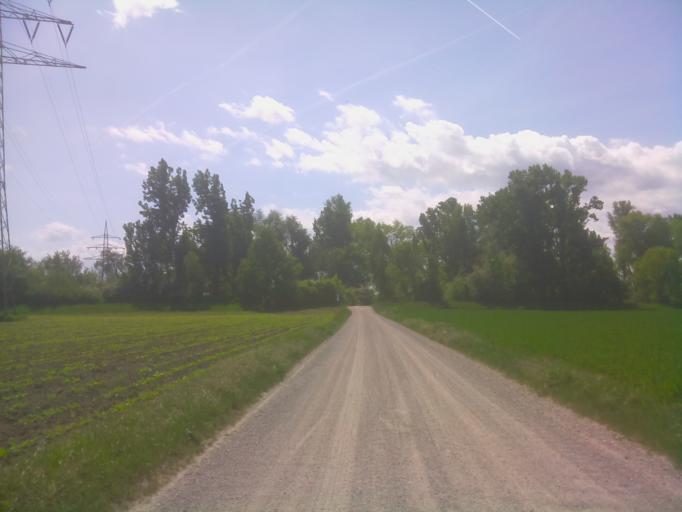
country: DE
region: Rheinland-Pfalz
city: Neuhofen
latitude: 49.4380
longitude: 8.4382
